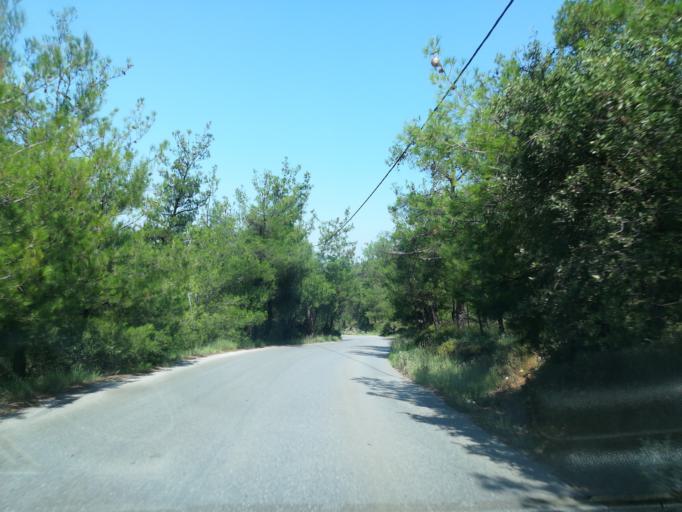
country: GR
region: Central Macedonia
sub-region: Nomos Thessalonikis
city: Agios Pavlos
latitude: 40.6429
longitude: 22.9792
